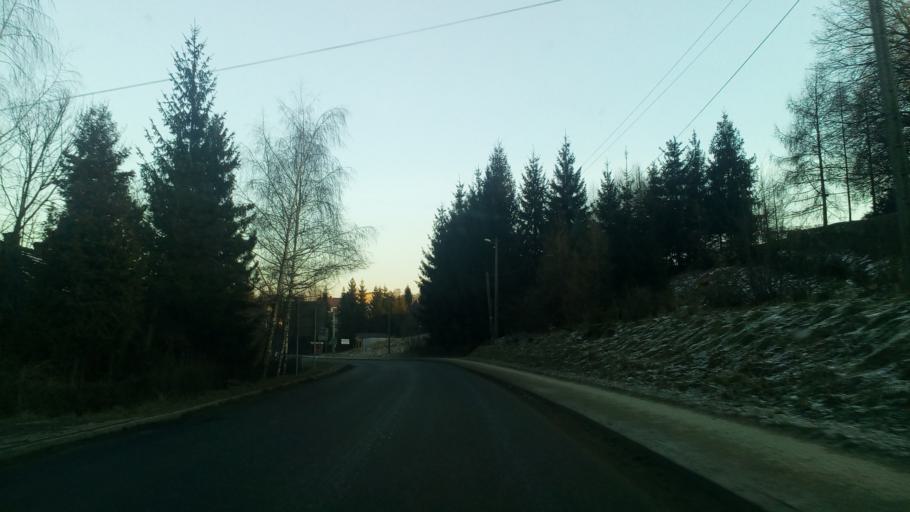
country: PL
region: Lesser Poland Voivodeship
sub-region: Powiat nowosadecki
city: Chelmiec
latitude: 49.6697
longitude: 20.6511
